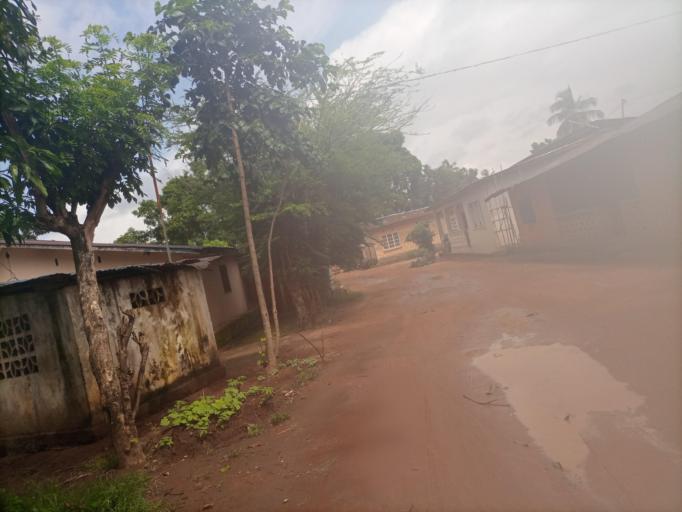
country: SL
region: Northern Province
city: Tintafor
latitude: 8.6300
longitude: -13.2153
